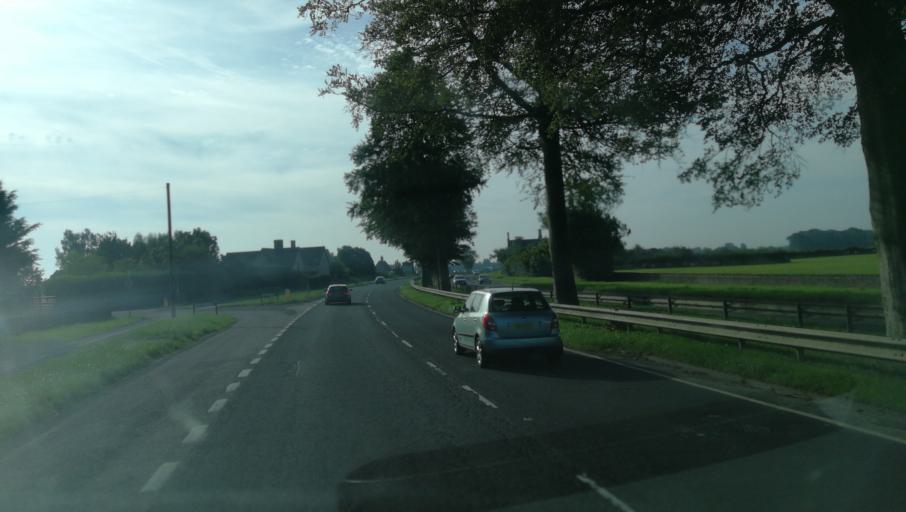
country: GB
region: England
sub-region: Oxfordshire
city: Woodstock
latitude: 51.8341
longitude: -1.3282
